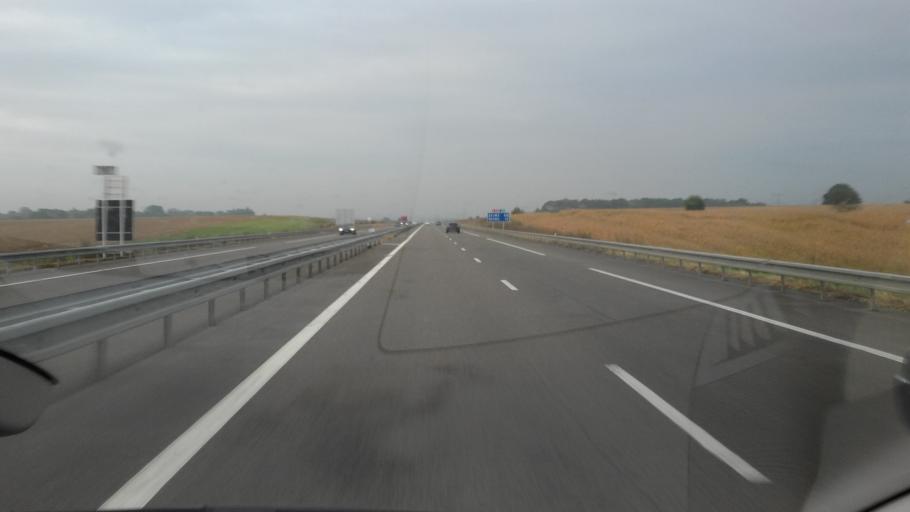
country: FR
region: Champagne-Ardenne
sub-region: Departement des Ardennes
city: Attigny
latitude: 49.5872
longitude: 4.4910
